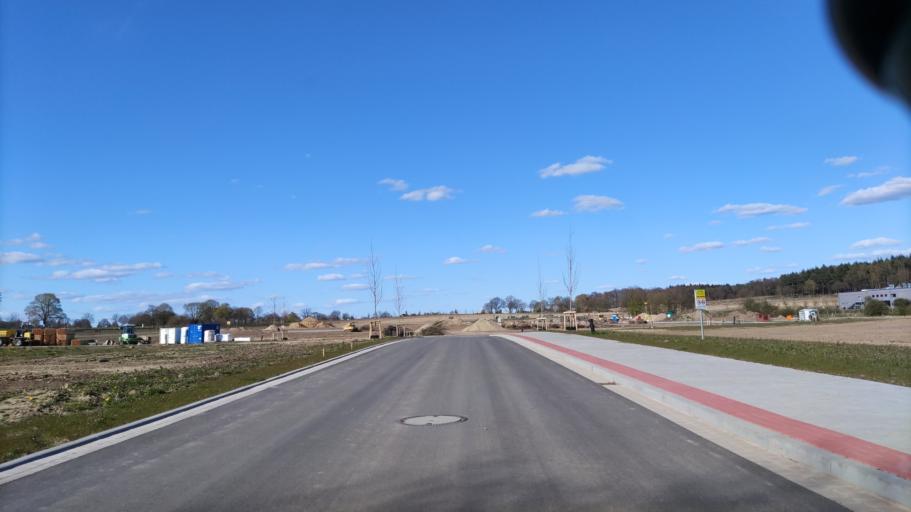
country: DE
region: Lower Saxony
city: Buchholz in der Nordheide
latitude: 53.3558
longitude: 9.8668
